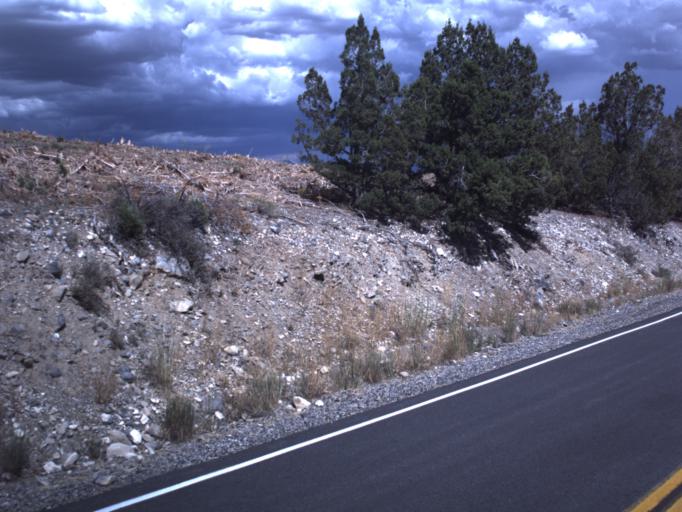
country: US
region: Utah
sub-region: Tooele County
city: Grantsville
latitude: 40.3335
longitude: -112.5229
